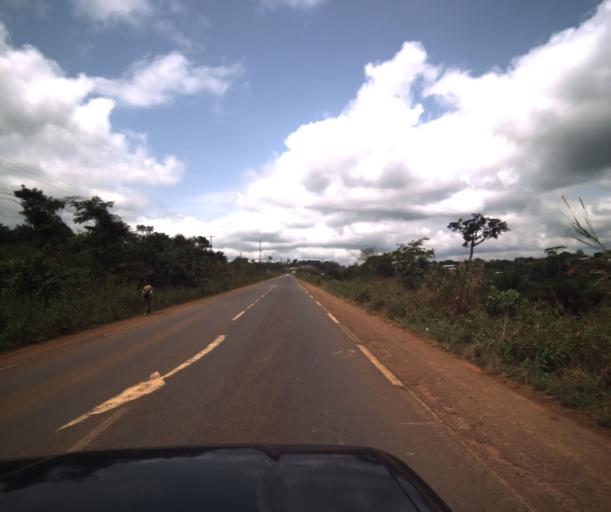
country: CM
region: Centre
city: Mbankomo
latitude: 3.7907
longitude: 11.4097
